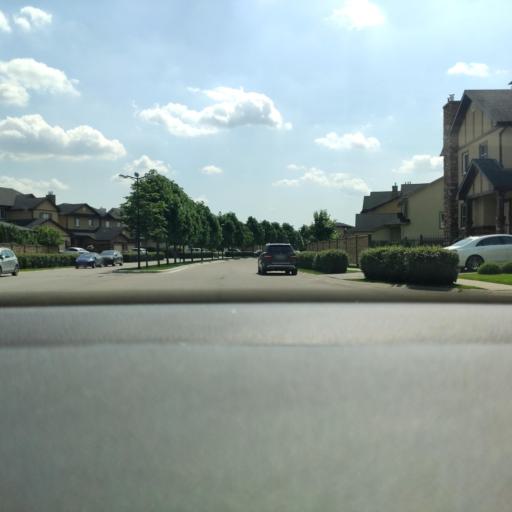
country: RU
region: Moscow
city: Lianozovo
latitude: 55.9272
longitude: 37.6016
